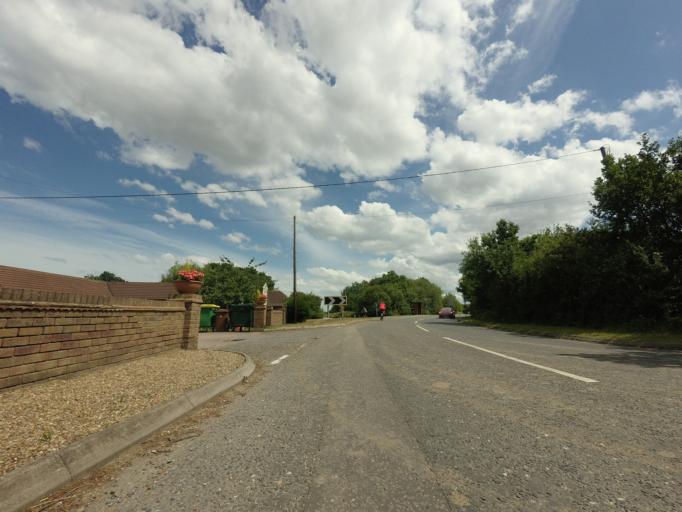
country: GB
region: England
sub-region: Medway
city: High Halstow
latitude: 51.4450
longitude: 0.5772
